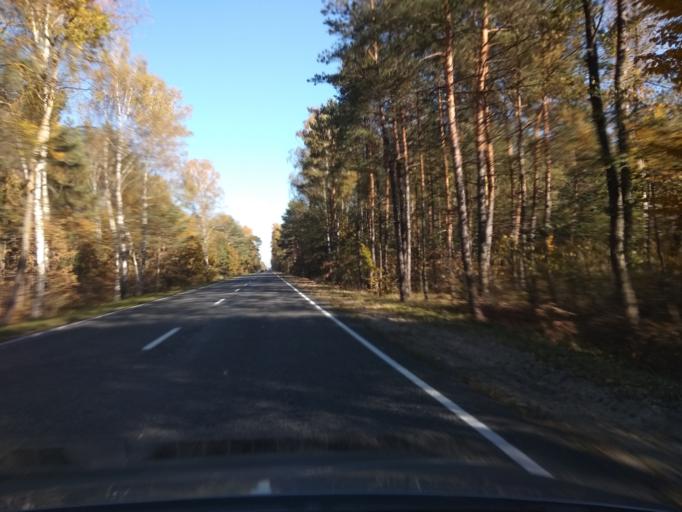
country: BY
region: Brest
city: Malaryta
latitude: 51.9225
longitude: 24.1615
